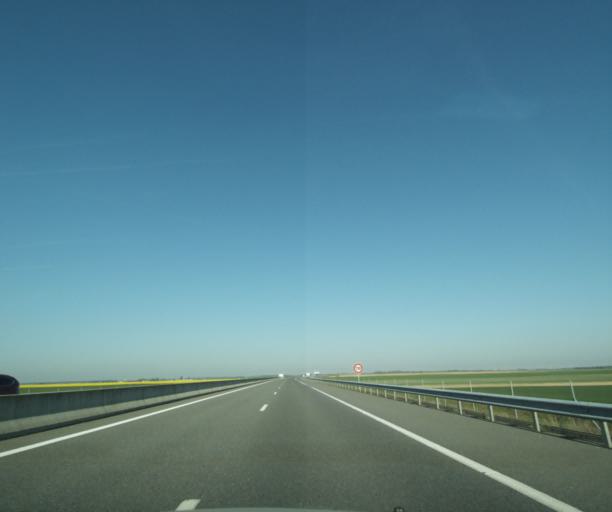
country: FR
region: Centre
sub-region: Departement du Loiret
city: Pannes
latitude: 48.0662
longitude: 2.6575
